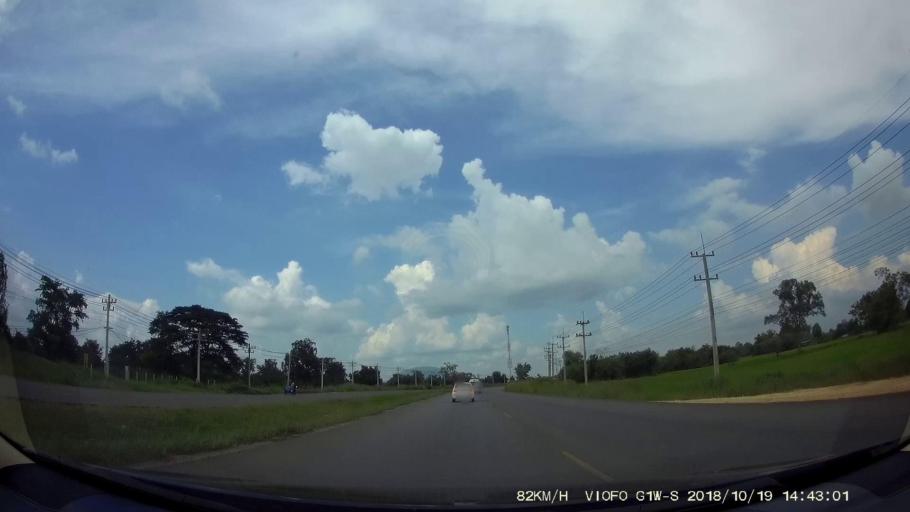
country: TH
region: Chaiyaphum
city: Phu Khiao
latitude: 16.2752
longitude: 102.2045
